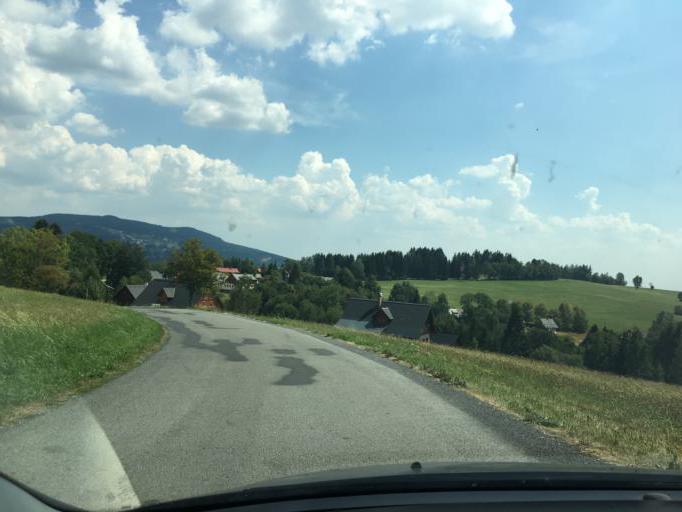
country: CZ
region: Liberecky
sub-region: Okres Semily
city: Ponikla
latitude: 50.6792
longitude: 15.5026
